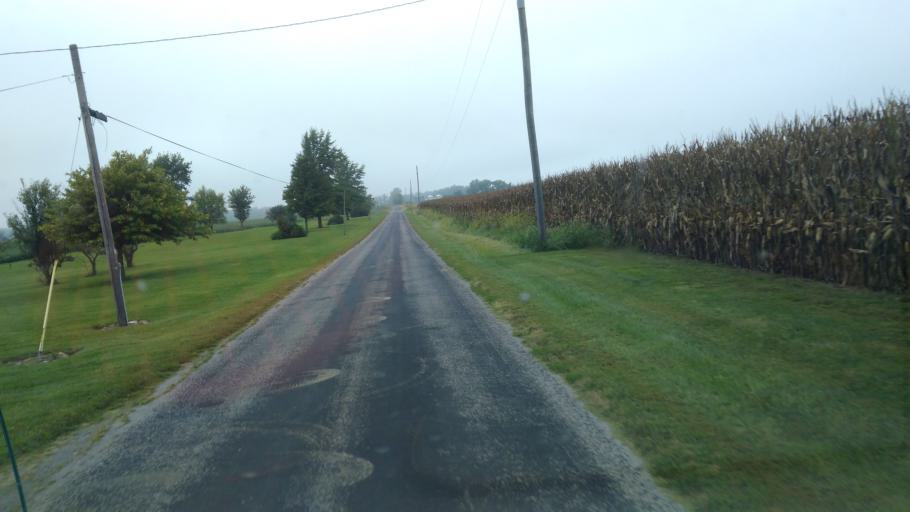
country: US
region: Ohio
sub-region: Hardin County
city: Kenton
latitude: 40.5196
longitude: -83.6006
